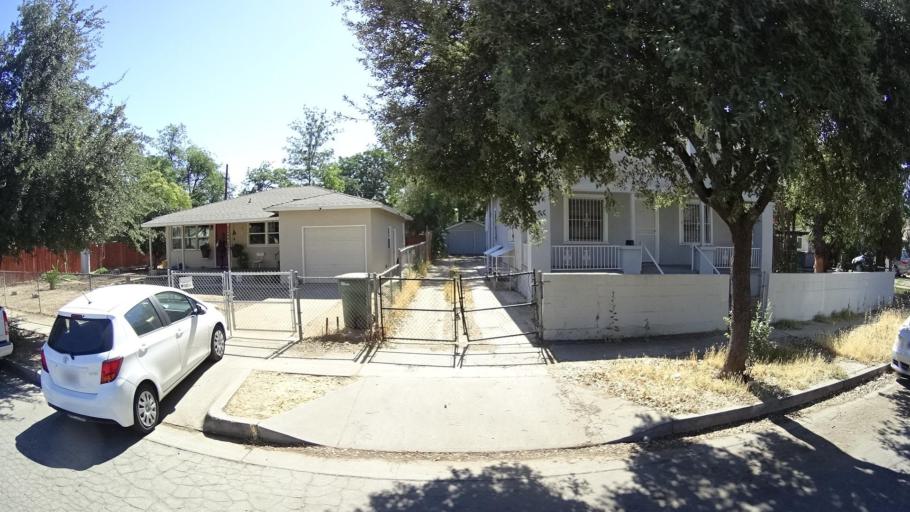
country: US
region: California
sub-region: Fresno County
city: Fresno
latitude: 36.7185
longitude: -119.7897
